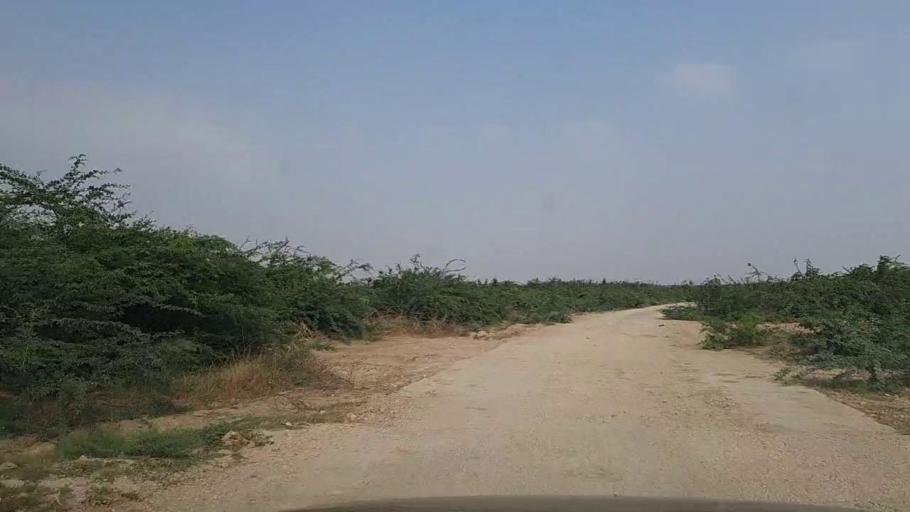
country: PK
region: Sindh
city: Thatta
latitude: 24.8657
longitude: 67.8078
